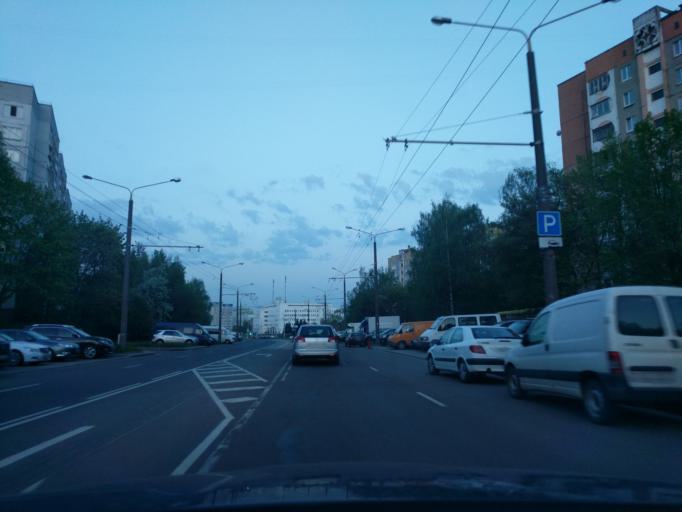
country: BY
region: Minsk
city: Novoye Medvezhino
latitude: 53.8995
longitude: 27.4484
